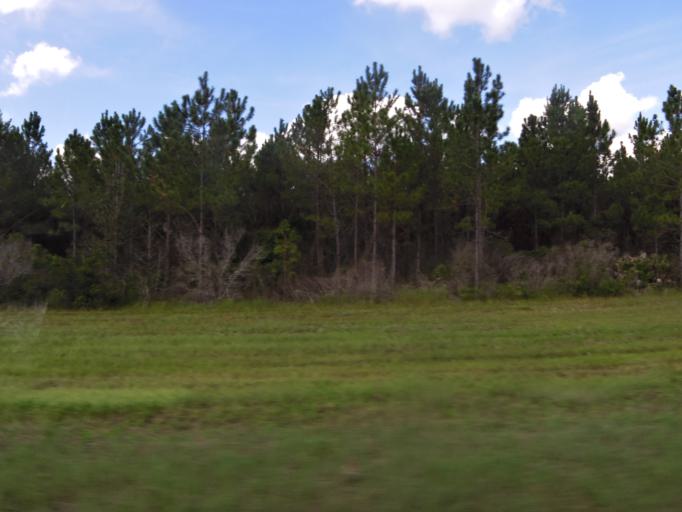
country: US
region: Florida
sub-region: Hamilton County
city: Jasper
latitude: 30.6749
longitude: -82.6417
